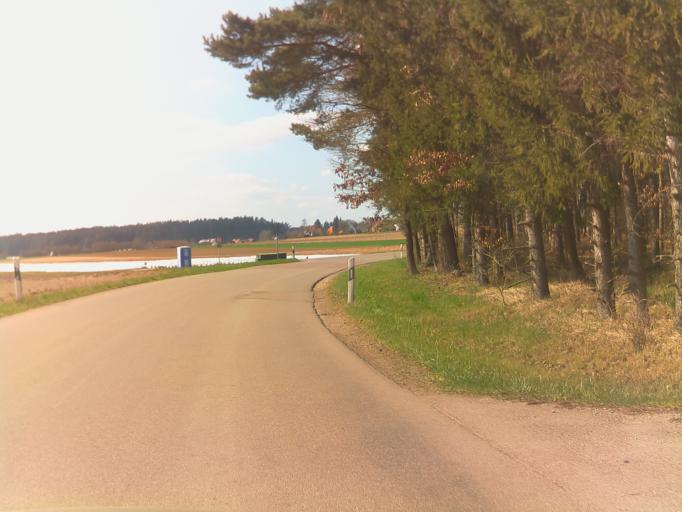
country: DE
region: Bavaria
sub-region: Swabia
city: Inchenhofen
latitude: 48.5425
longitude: 11.1310
